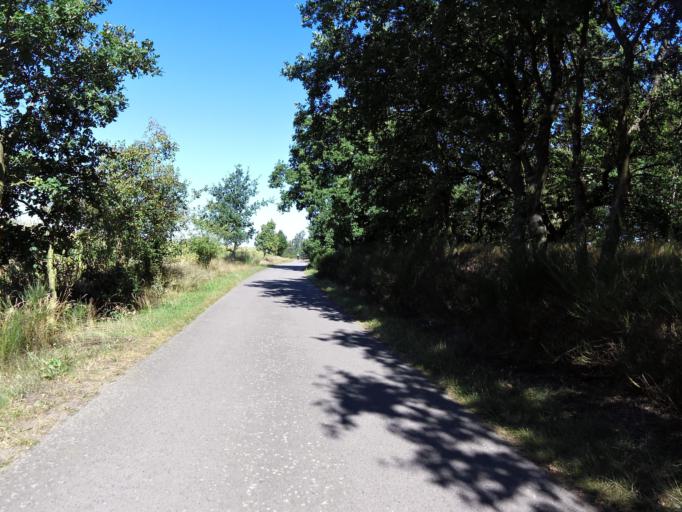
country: DE
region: Saxony
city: Dommitzsch
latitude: 51.6674
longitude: 12.8338
